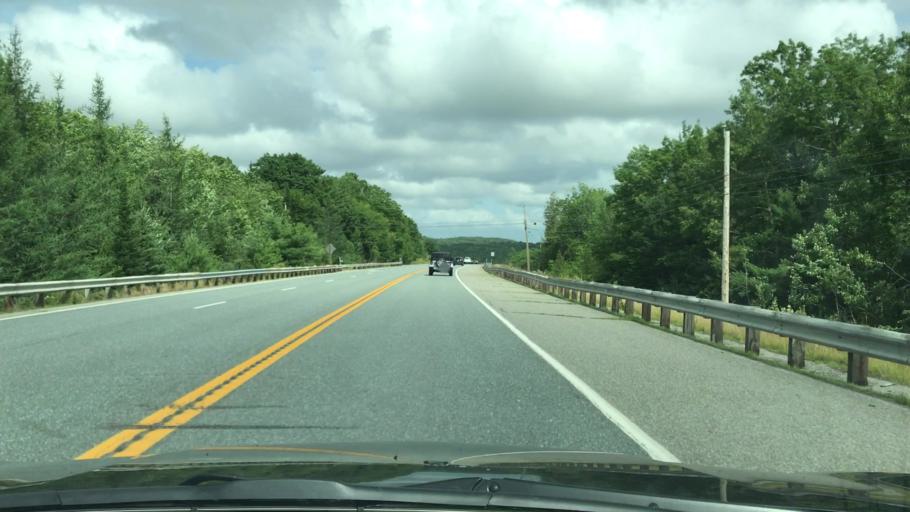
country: US
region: Maine
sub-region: Hancock County
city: Orland
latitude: 44.5679
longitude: -68.6275
